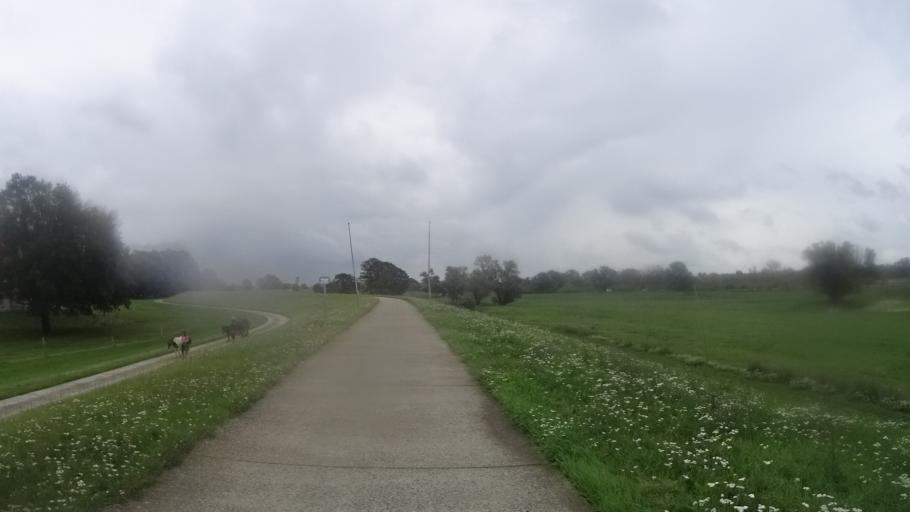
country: DE
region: Lower Saxony
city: Bleckede
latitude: 53.2987
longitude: 10.7494
